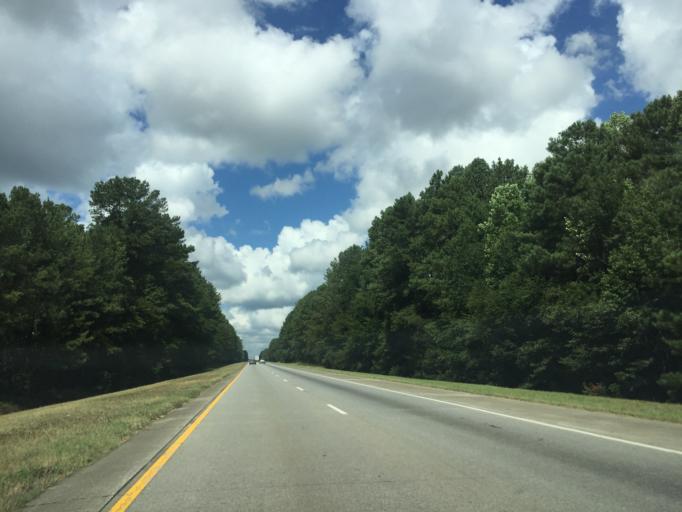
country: US
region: Georgia
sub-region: Candler County
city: Metter
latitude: 32.3851
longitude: -82.2460
